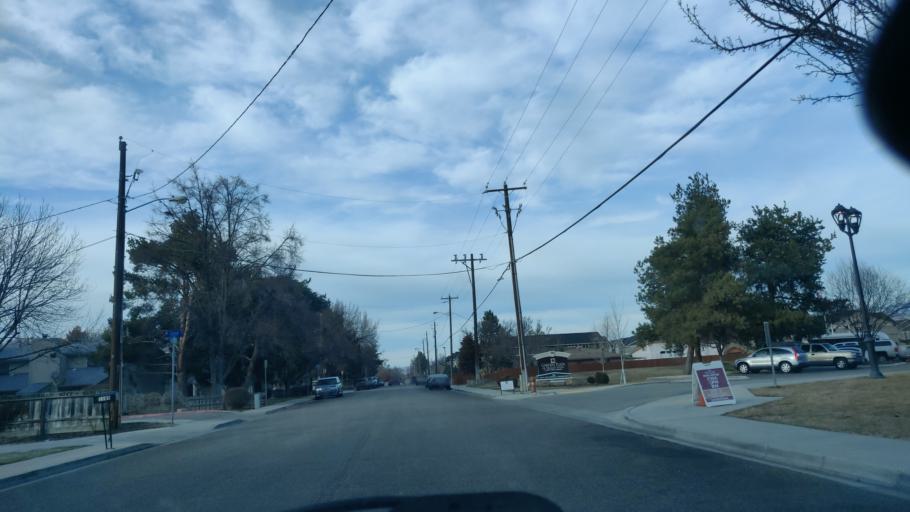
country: US
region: Idaho
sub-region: Ada County
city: Garden City
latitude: 43.6147
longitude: -116.2662
